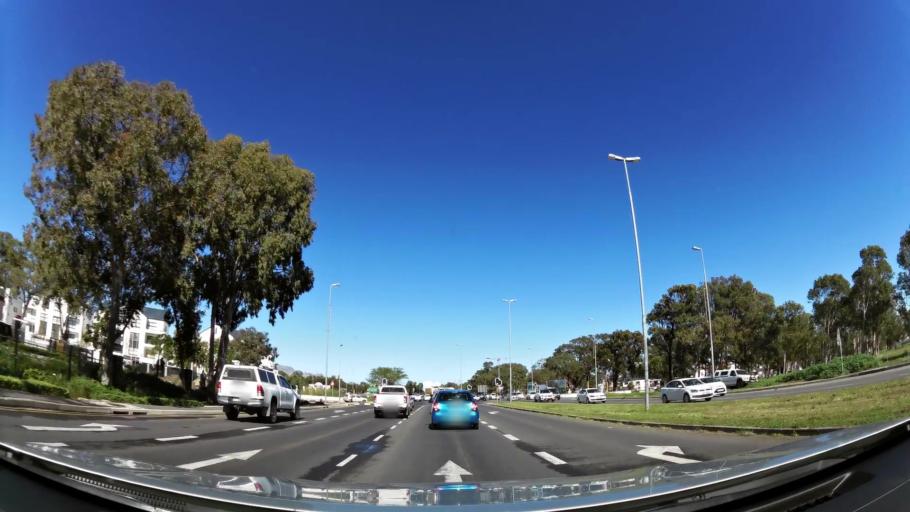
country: ZA
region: Western Cape
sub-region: Cape Winelands District Municipality
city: Stellenbosch
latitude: -34.0894
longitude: 18.8195
